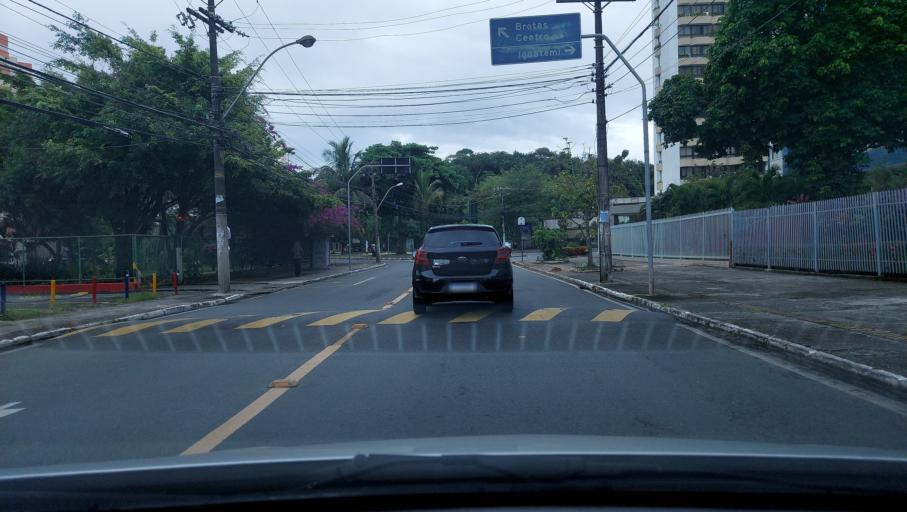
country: BR
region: Bahia
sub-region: Salvador
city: Salvador
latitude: -12.9935
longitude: -38.4632
